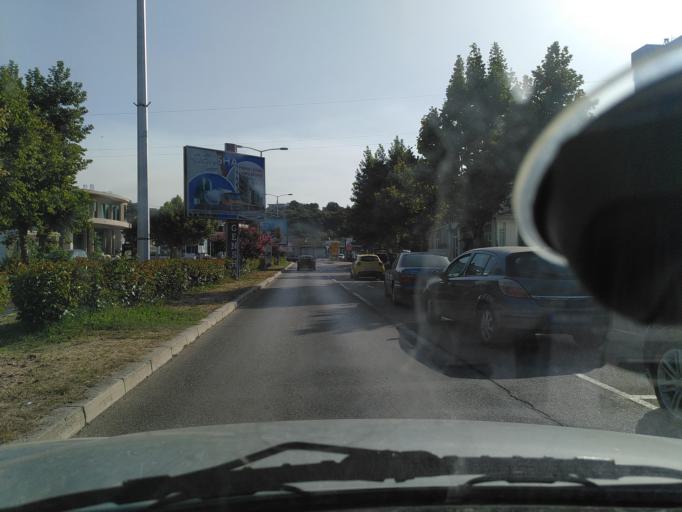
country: ME
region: Ulcinj
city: Ulcinj
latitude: 41.9326
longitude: 19.2215
